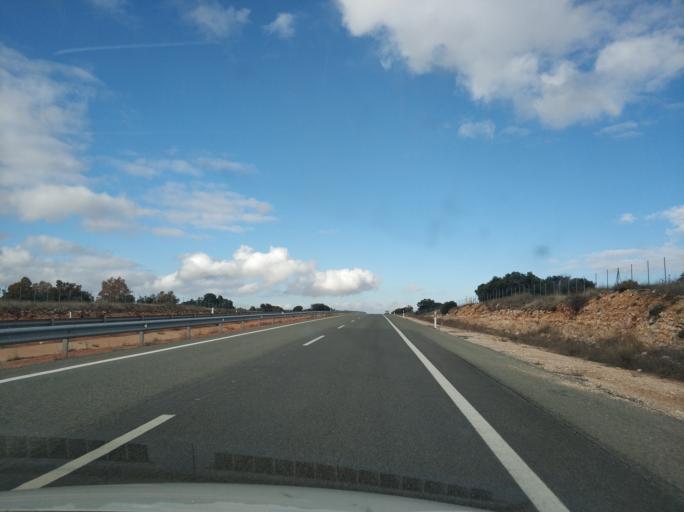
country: ES
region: Castille and Leon
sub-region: Provincia de Soria
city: Adradas
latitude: 41.3004
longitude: -2.4785
